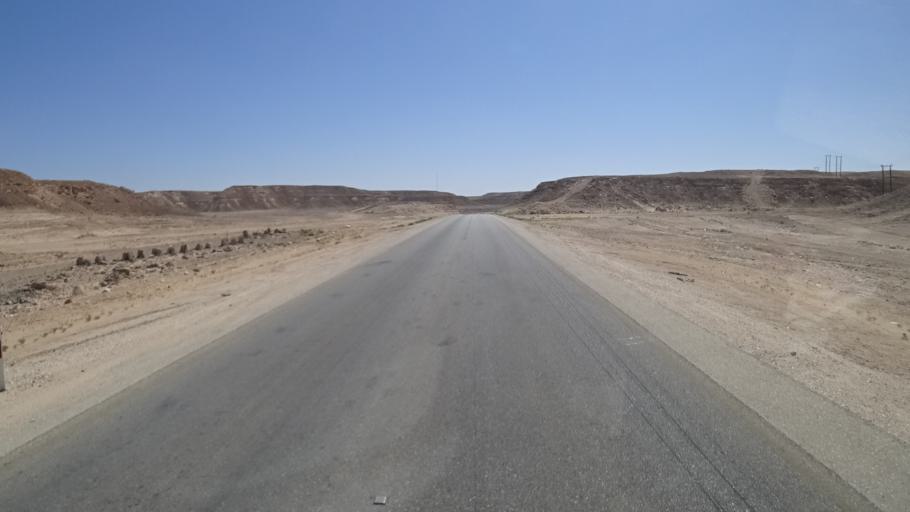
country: OM
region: Zufar
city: Salalah
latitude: 17.4986
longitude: 53.3623
